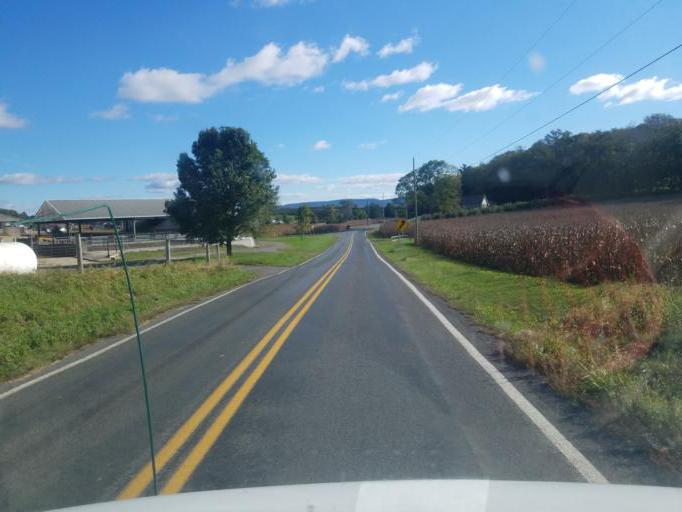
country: US
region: Pennsylvania
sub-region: Franklin County
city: Guilford Siding
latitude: 39.8117
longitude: -77.6309
